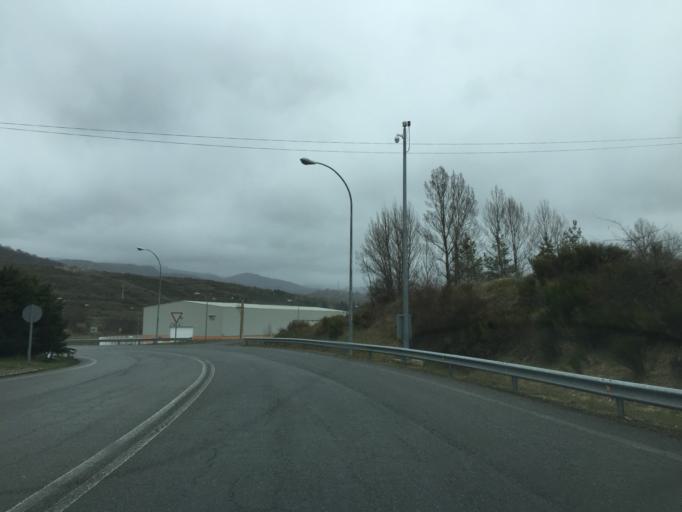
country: ES
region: Castille and Leon
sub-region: Provincia de Leon
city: Carrocera
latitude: 42.7831
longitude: -5.7833
